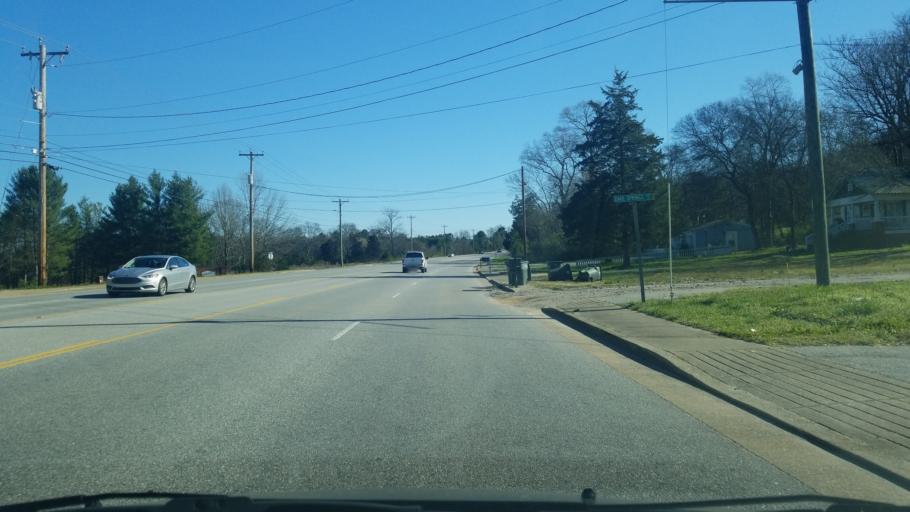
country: US
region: Tennessee
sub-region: Hamilton County
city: Middle Valley
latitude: 35.1642
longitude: -85.1897
